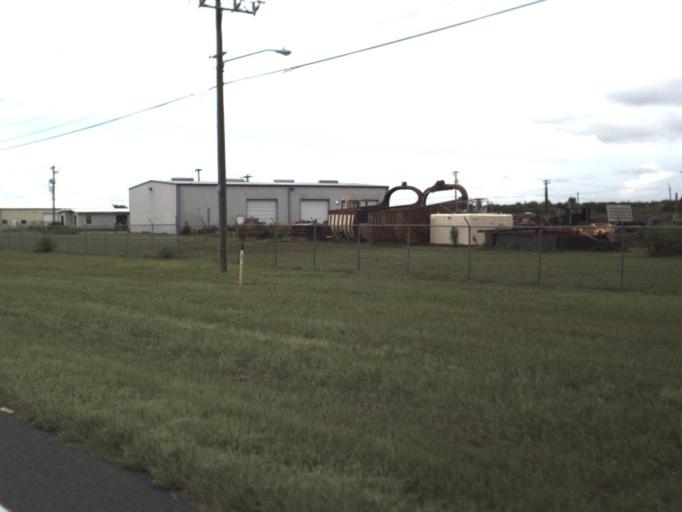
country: US
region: Florida
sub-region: Polk County
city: Bartow
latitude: 27.8415
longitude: -81.8243
